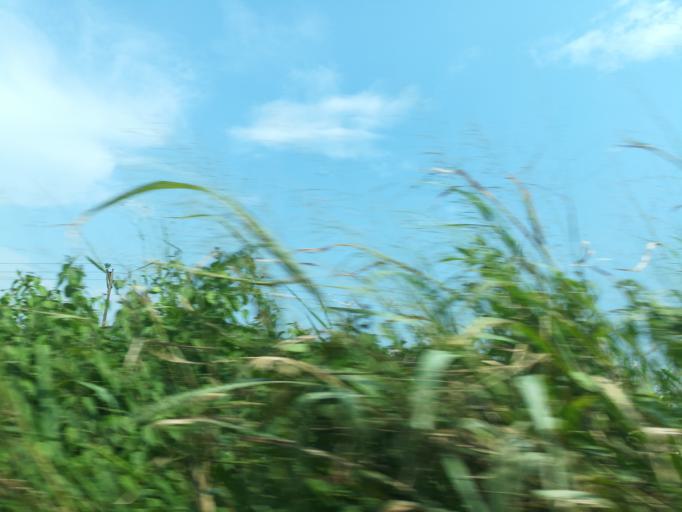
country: NG
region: Lagos
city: Ikorodu
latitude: 6.6122
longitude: 3.6420
